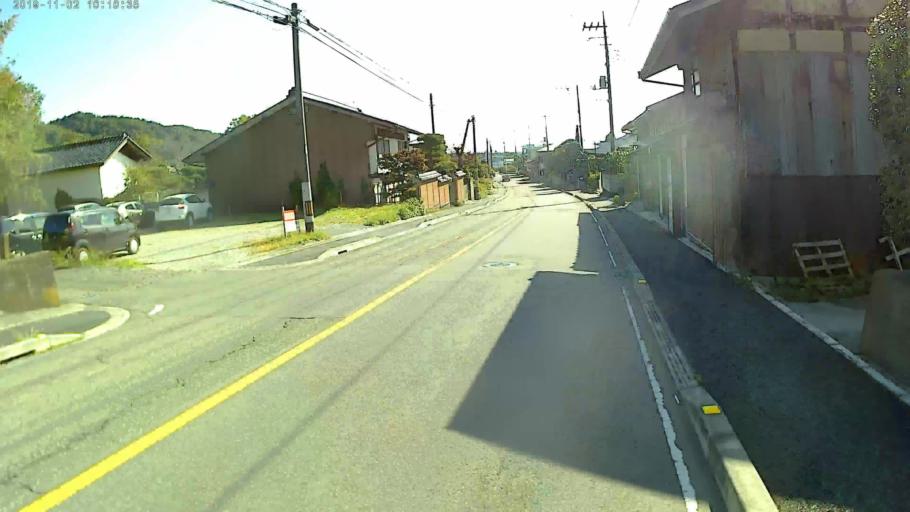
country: JP
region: Gunma
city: Annaka
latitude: 36.3175
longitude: 138.7902
